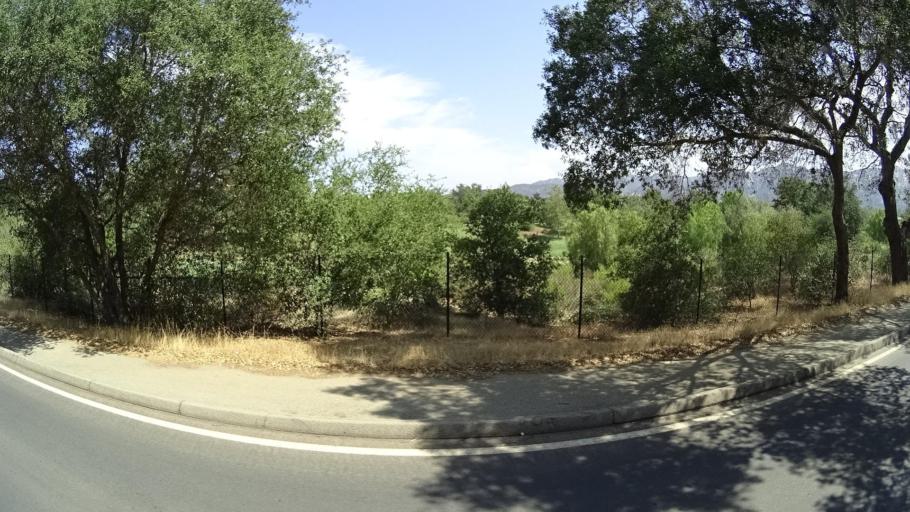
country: US
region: California
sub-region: San Diego County
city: Escondido
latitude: 33.1695
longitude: -117.0944
